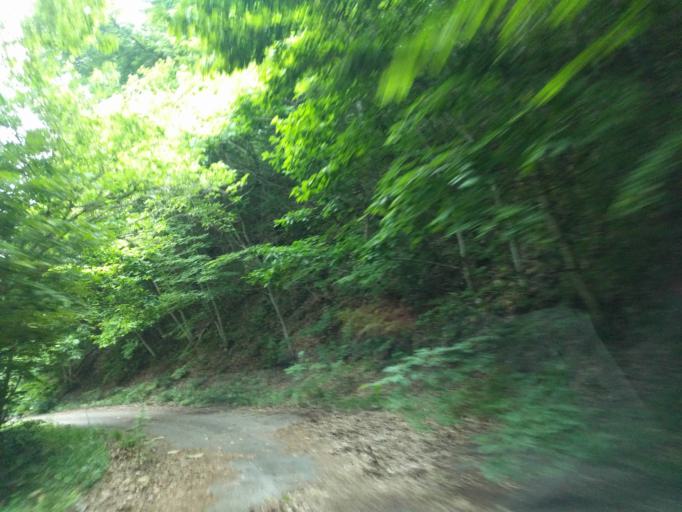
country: JP
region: Fukushima
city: Inawashiro
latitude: 37.4442
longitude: 140.0314
